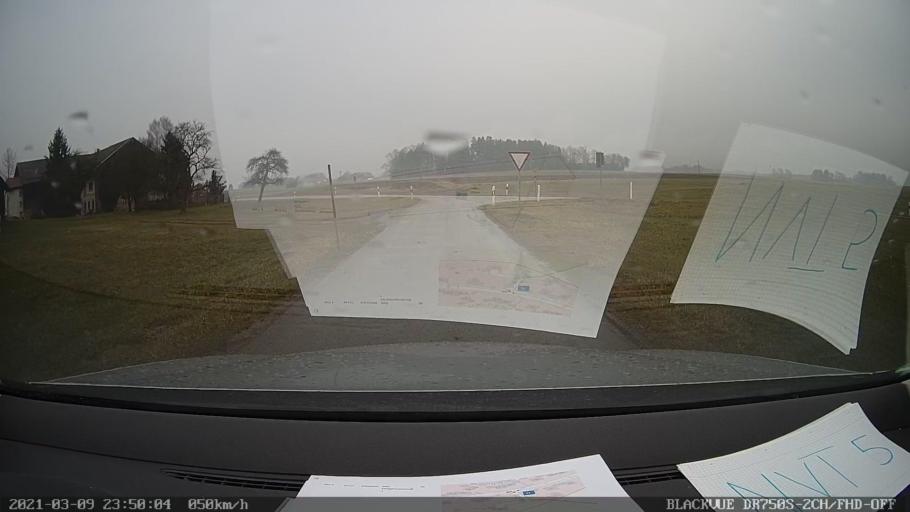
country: DE
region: Bavaria
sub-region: Upper Bavaria
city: Schonstett
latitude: 47.9811
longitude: 12.2563
